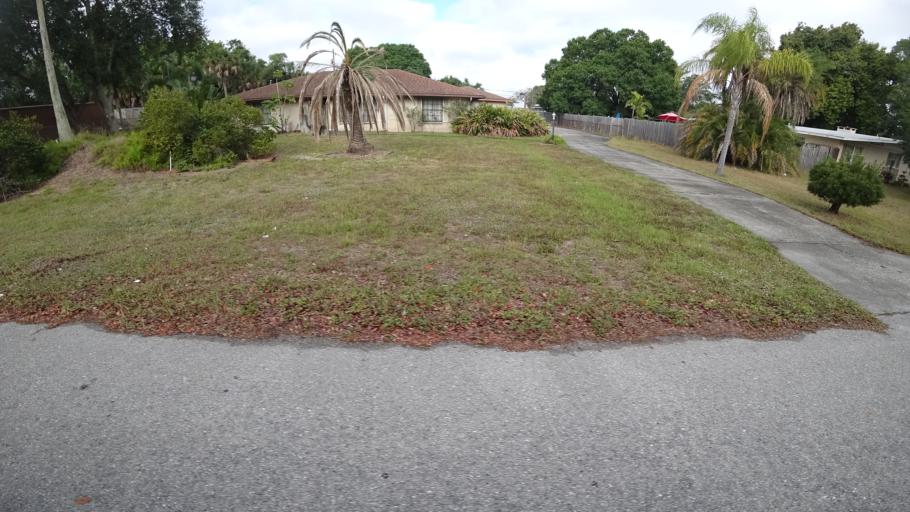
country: US
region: Florida
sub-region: Manatee County
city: Bayshore Gardens
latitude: 27.4410
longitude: -82.5890
